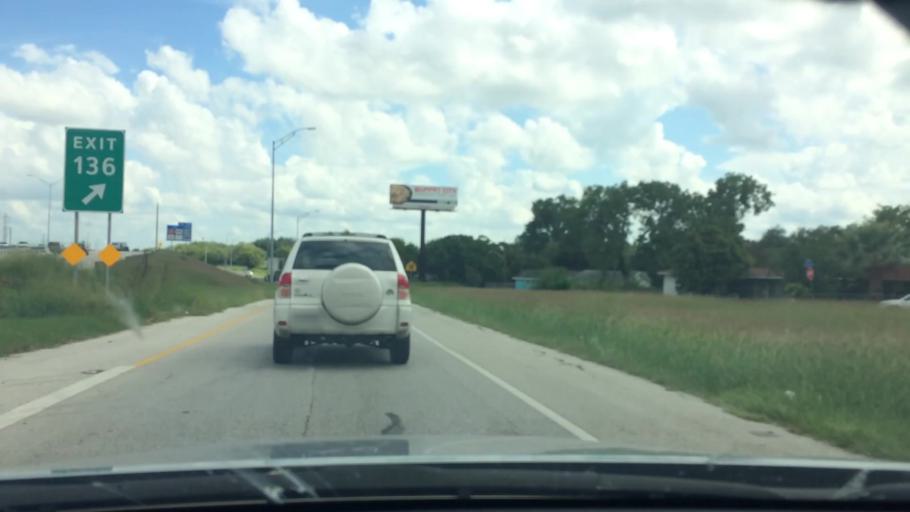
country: US
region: Texas
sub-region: Bexar County
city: San Antonio
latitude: 29.3633
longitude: -98.4450
